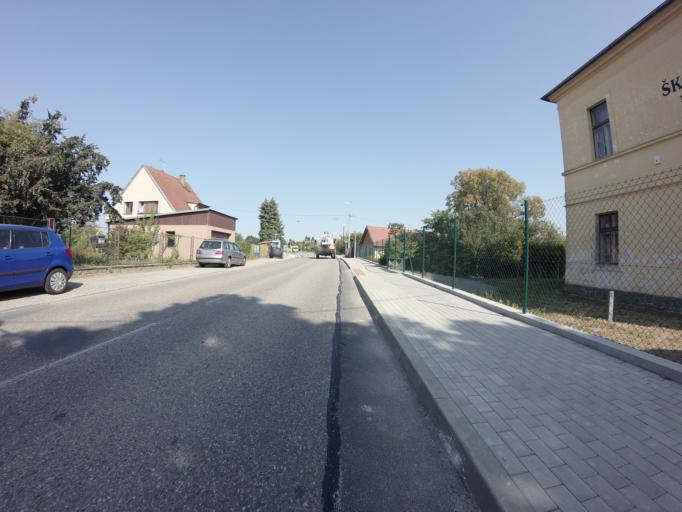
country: CZ
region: Central Bohemia
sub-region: Okres Benesov
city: Benesov
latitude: 49.8001
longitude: 14.6550
